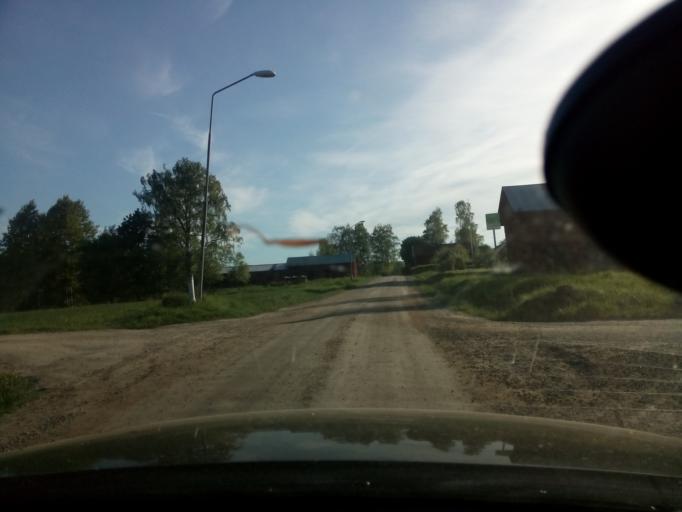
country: SE
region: Soedermanland
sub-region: Nykopings Kommun
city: Nykoping
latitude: 58.9148
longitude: 17.0005
